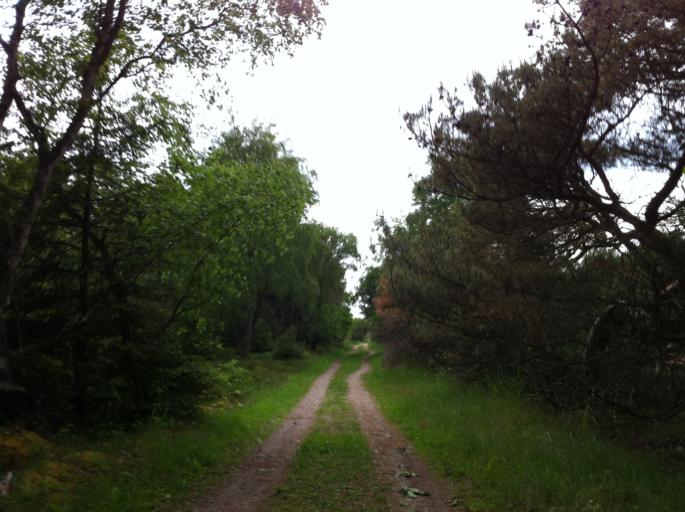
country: DK
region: Capital Region
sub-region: Halsnaes Kommune
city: Frederiksvaerk
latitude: 56.0400
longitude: 12.0346
